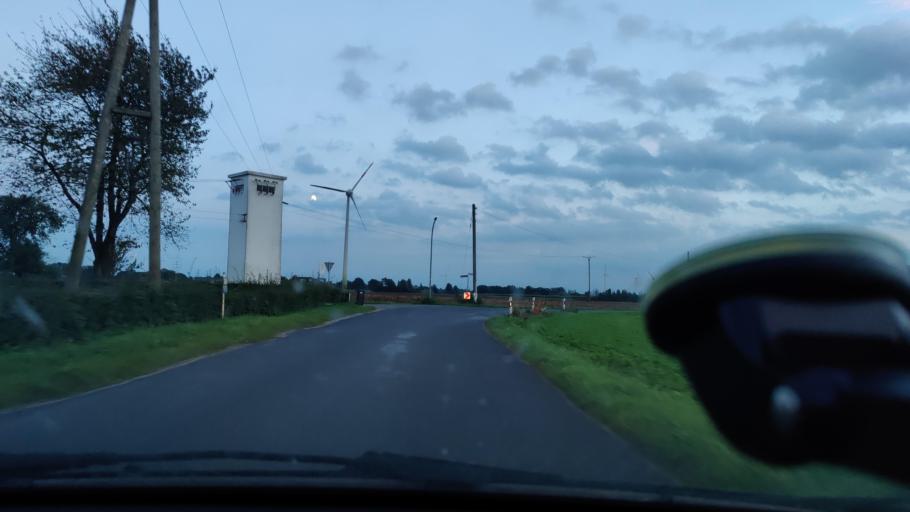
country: DE
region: North Rhine-Westphalia
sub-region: Regierungsbezirk Dusseldorf
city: Goch
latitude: 51.7292
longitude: 6.1972
